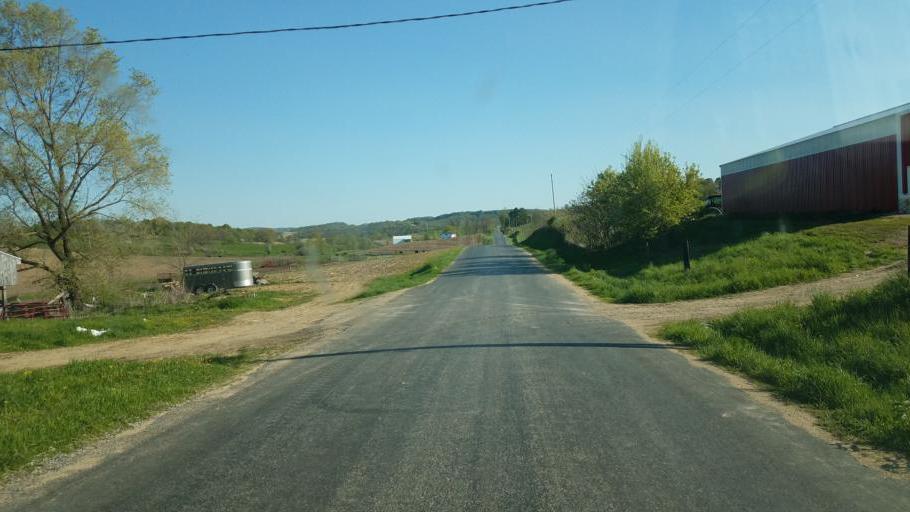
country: US
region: Wisconsin
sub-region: Vernon County
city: Hillsboro
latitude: 43.6780
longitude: -90.3774
